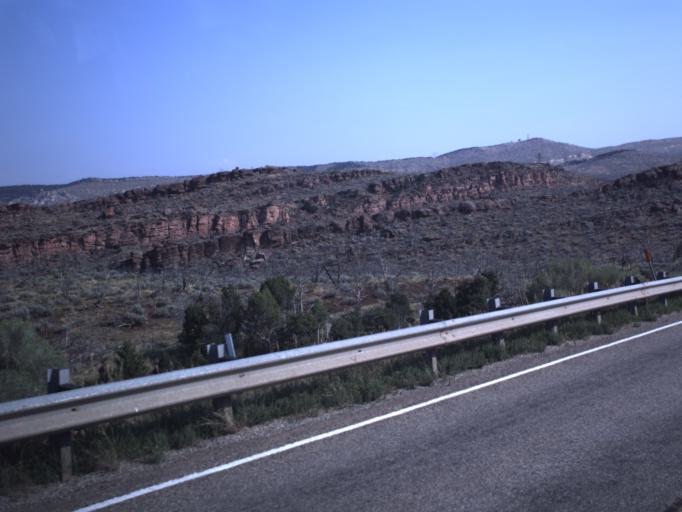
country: US
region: Utah
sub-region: Daggett County
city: Manila
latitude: 40.9256
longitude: -109.4164
